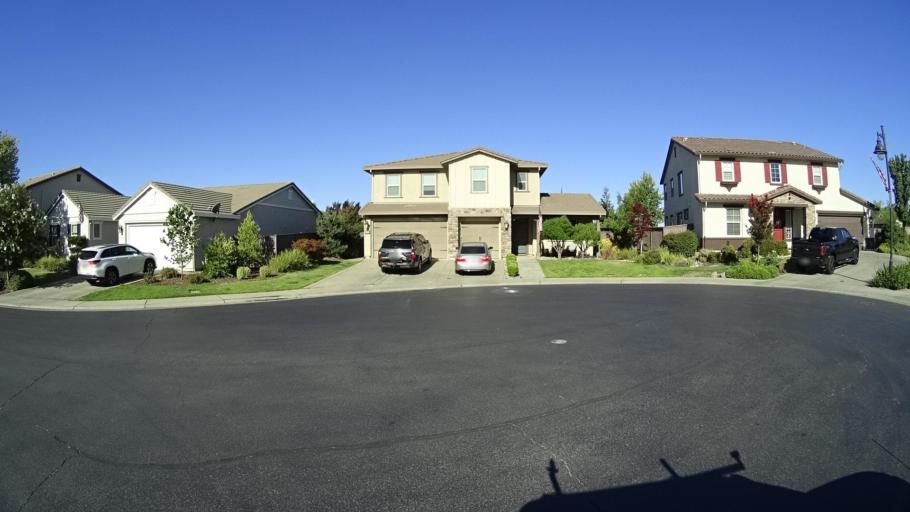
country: US
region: California
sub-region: Placer County
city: Rocklin
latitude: 38.8269
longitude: -121.2777
